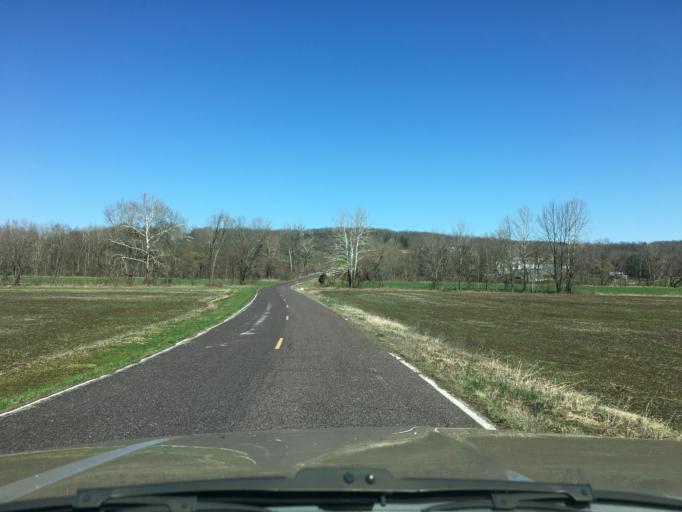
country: US
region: Missouri
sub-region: Franklin County
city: Gerald
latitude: 38.5258
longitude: -91.3303
